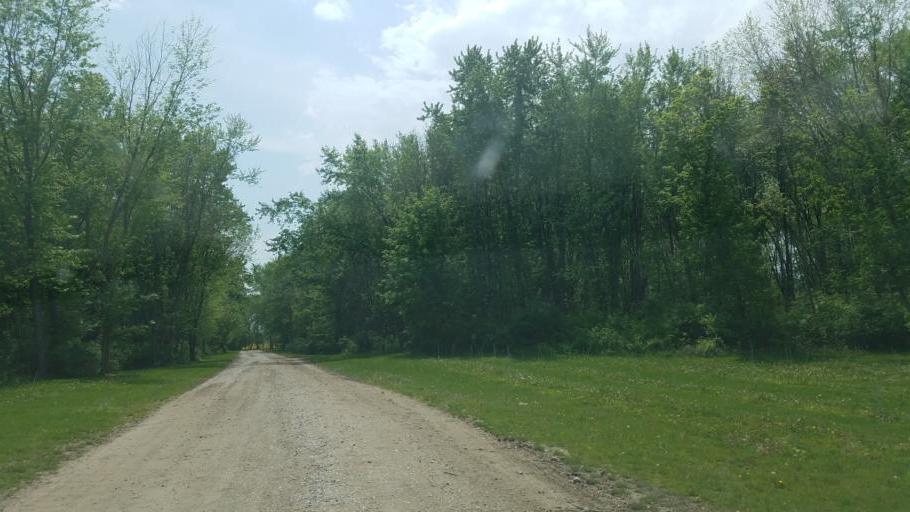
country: US
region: Ohio
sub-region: Fairfield County
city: Fairfield Beach
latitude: 39.9230
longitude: -82.4672
